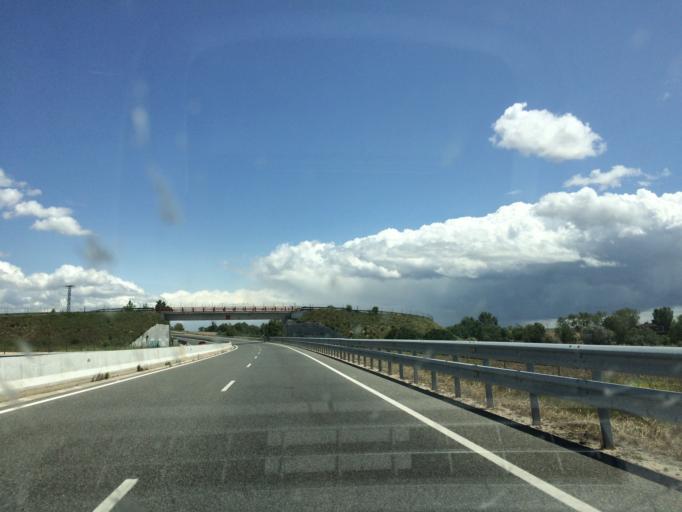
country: ES
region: Madrid
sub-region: Provincia de Madrid
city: Fuente el Saz
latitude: 40.6332
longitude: -3.5355
